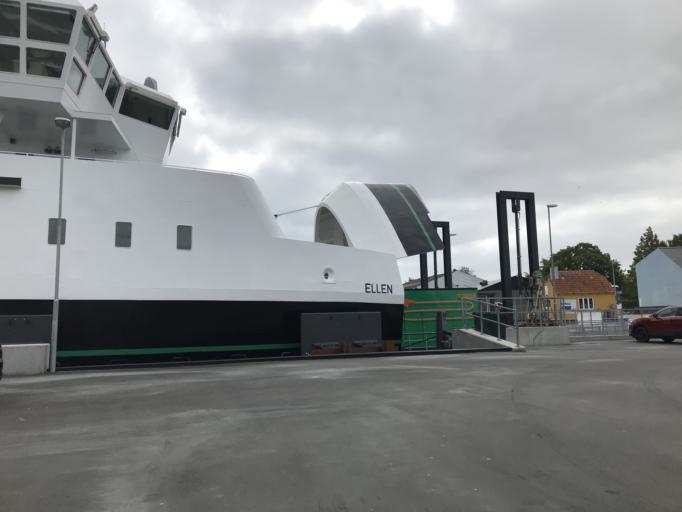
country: DK
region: South Denmark
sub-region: Faaborg-Midtfyn Kommune
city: Faaborg
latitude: 54.9416
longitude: 10.2587
